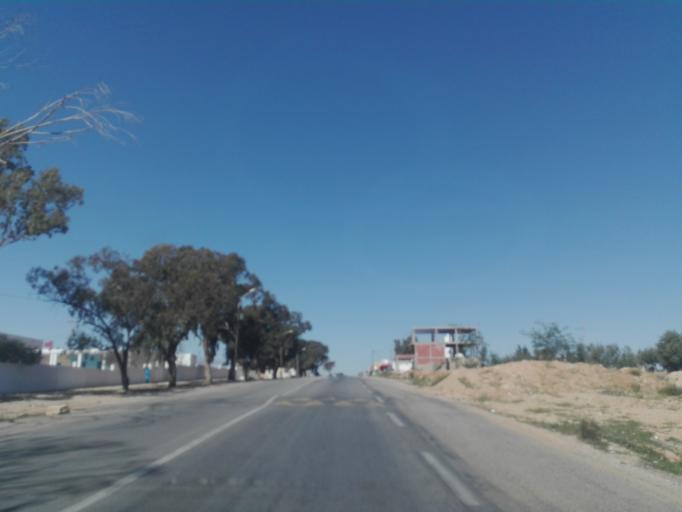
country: TN
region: Safaqis
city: Bi'r `Ali Bin Khalifah
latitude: 34.7413
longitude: 10.3735
